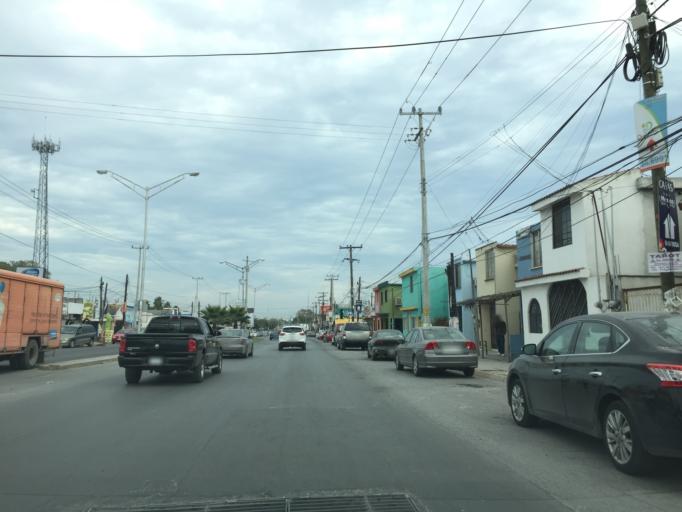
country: MX
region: Nuevo Leon
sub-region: Juarez
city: Valle de Juarez
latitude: 25.6623
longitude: -100.1773
